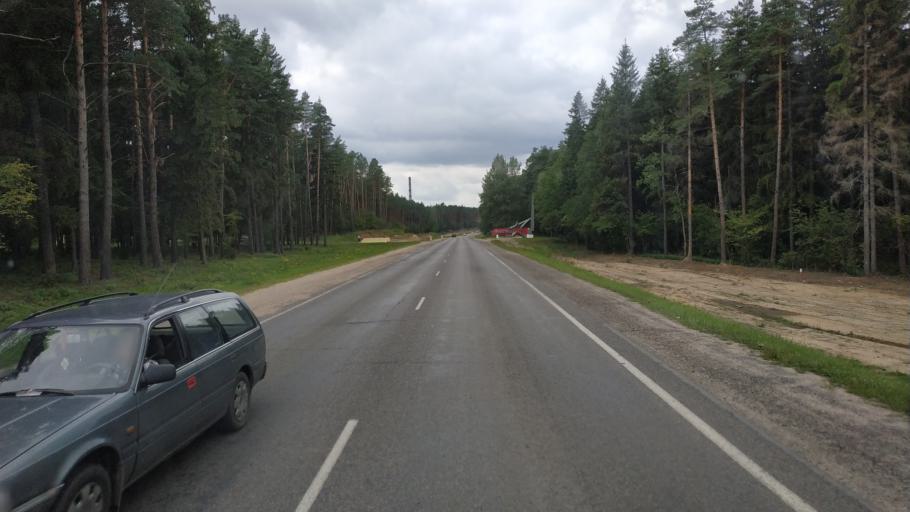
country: BY
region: Mogilev
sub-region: Mahilyowski Rayon
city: Veyno
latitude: 53.8765
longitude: 30.4240
